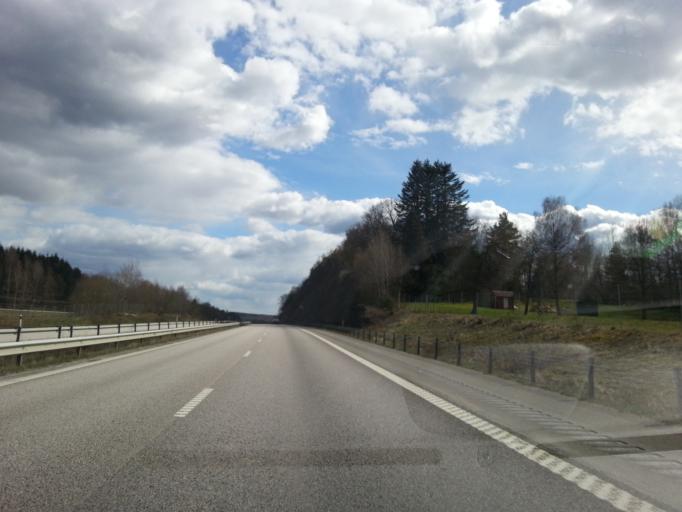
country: SE
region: Vaestra Goetaland
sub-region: Uddevalla Kommun
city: Ljungskile
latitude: 58.2579
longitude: 11.8997
